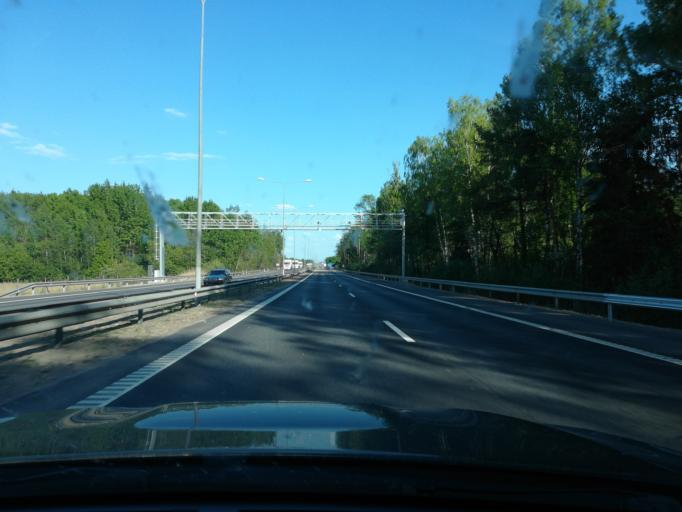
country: LT
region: Kauno apskritis
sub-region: Kauno rajonas
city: Karmelava
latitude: 54.8840
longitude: 24.1892
